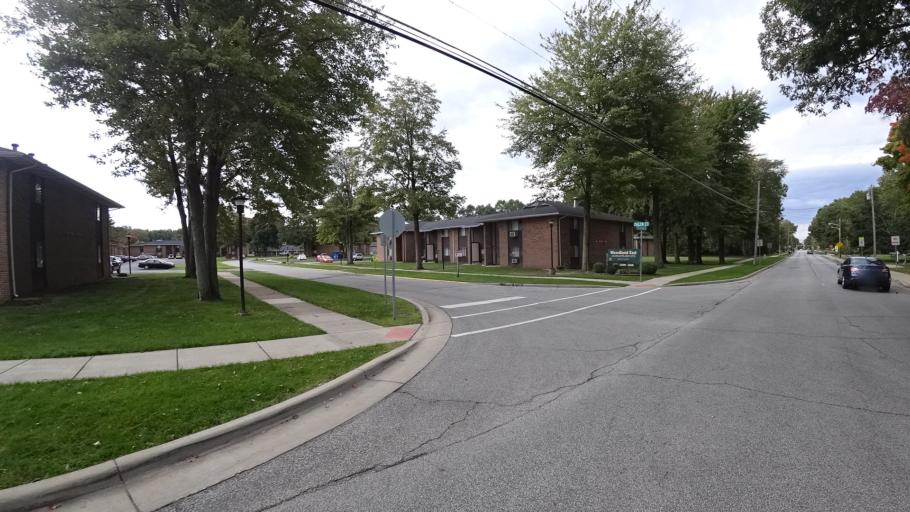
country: US
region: Indiana
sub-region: LaPorte County
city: Trail Creek
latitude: 41.6946
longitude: -86.8678
